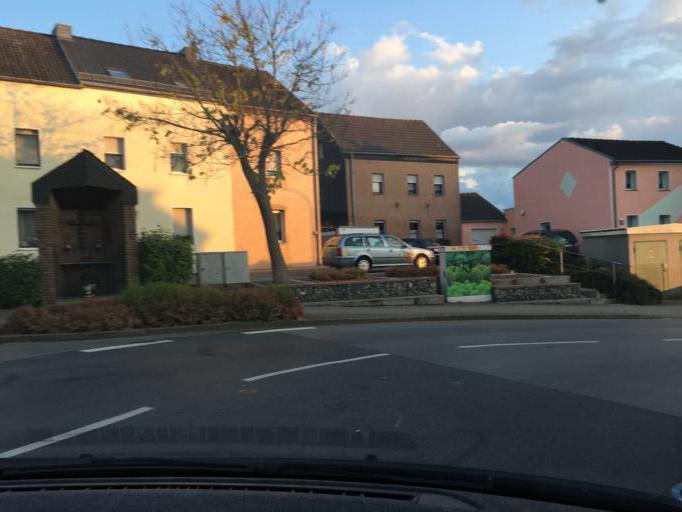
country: DE
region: North Rhine-Westphalia
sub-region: Regierungsbezirk Koln
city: Niederzier
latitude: 50.8528
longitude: 6.4594
